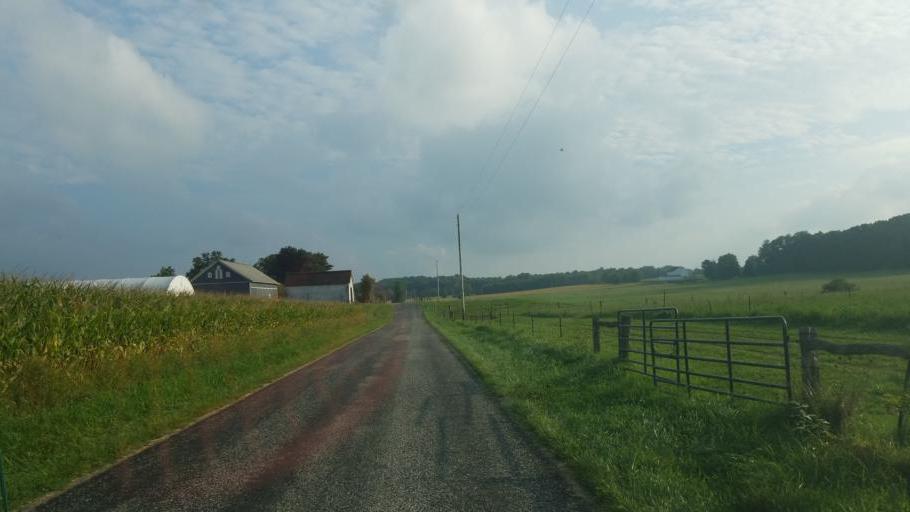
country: US
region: Ohio
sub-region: Wayne County
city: Wooster
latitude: 40.8639
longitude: -82.0295
